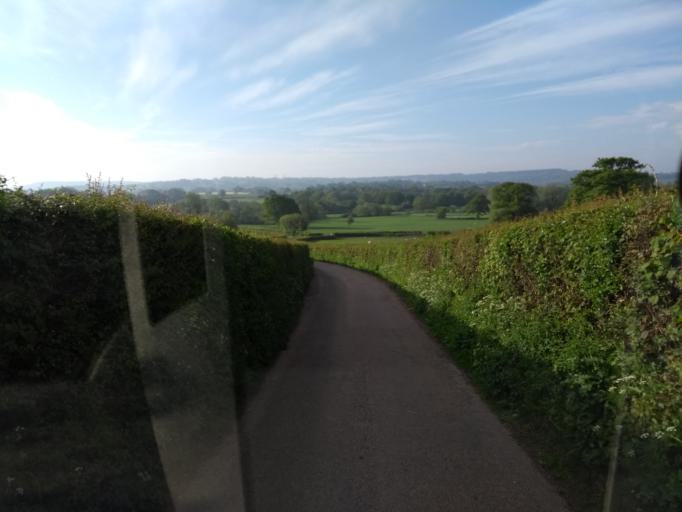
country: GB
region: England
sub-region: Devon
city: Axminster
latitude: 50.8203
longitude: -2.9618
